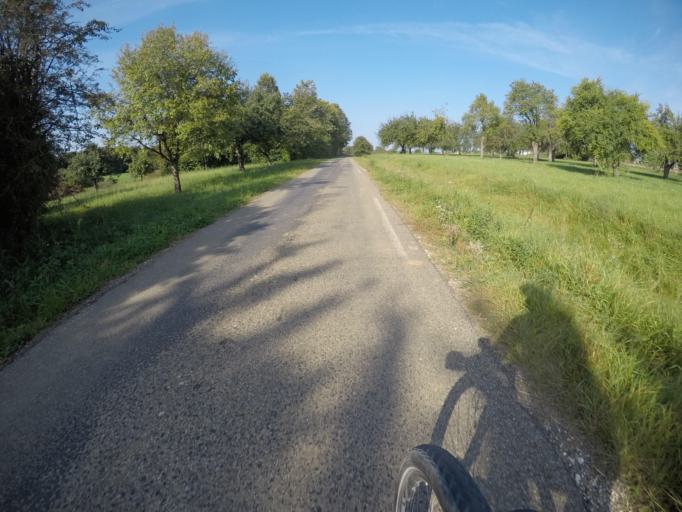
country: DE
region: Baden-Wuerttemberg
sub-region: Regierungsbezirk Stuttgart
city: Bohmenkirch
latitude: 48.6361
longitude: 9.9700
